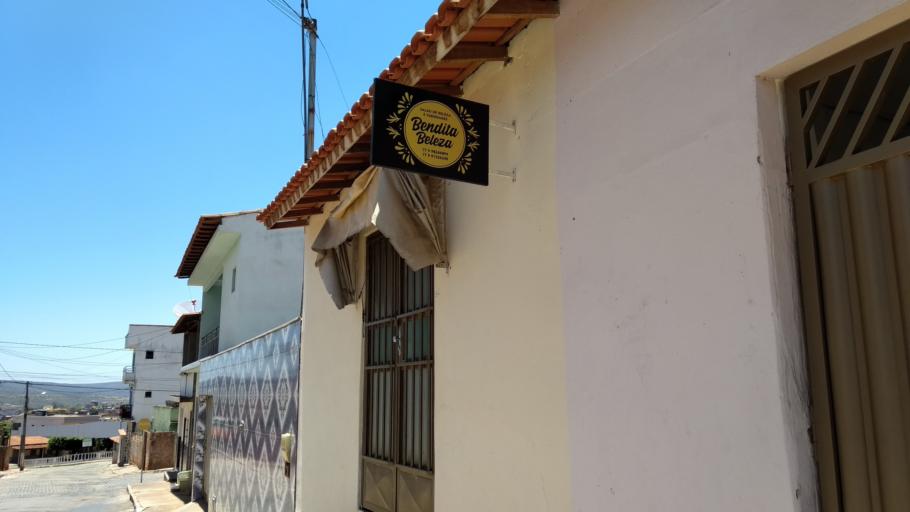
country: BR
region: Bahia
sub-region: Caetite
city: Caetite
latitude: -14.0591
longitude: -42.4830
